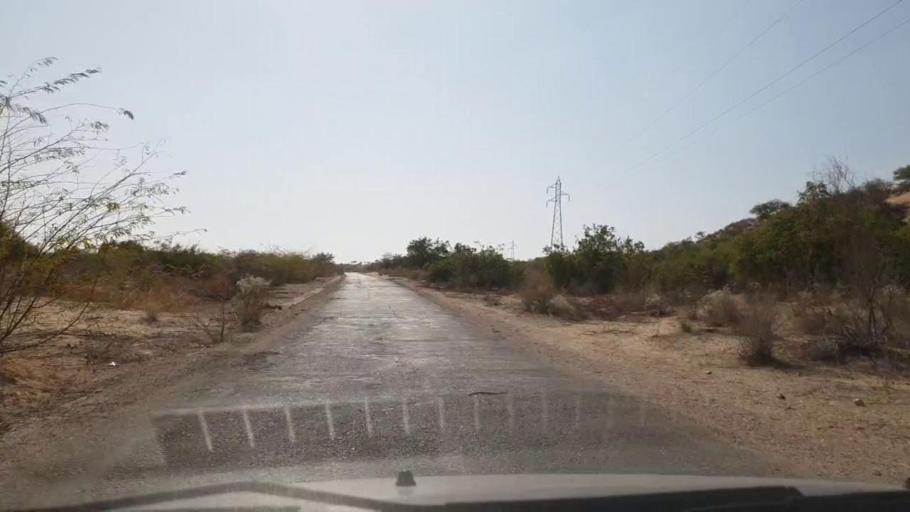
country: PK
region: Sindh
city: Mithi
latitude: 24.6390
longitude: 69.7435
